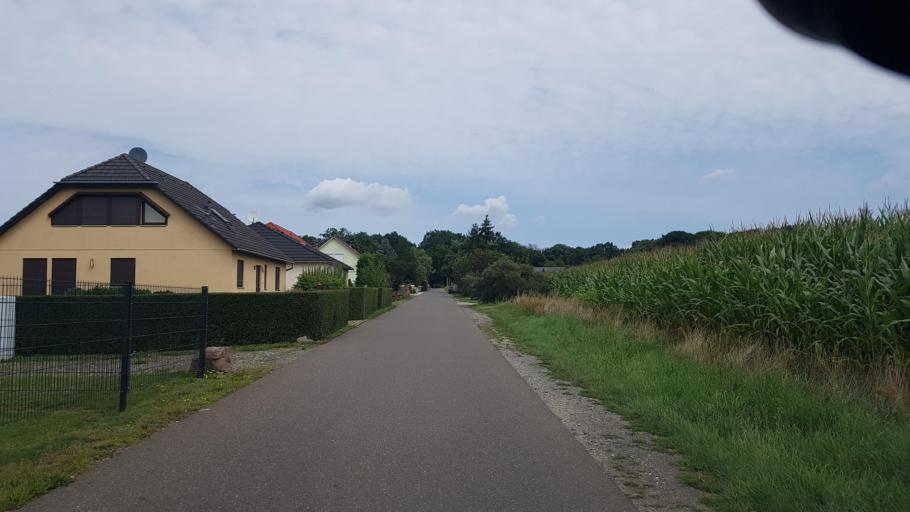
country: DE
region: Brandenburg
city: Spremberg
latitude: 51.5925
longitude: 14.3460
